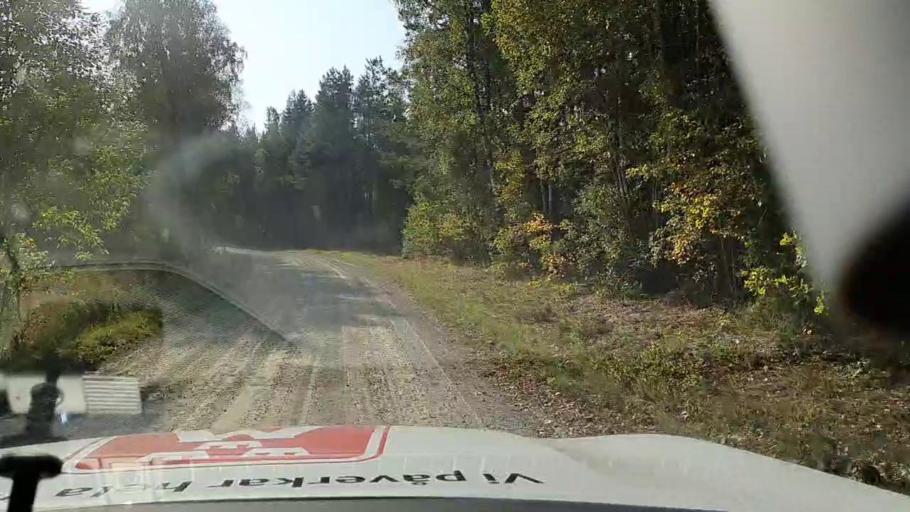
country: SE
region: Soedermanland
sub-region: Eskilstuna Kommun
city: Kvicksund
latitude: 59.3262
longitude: 16.2352
